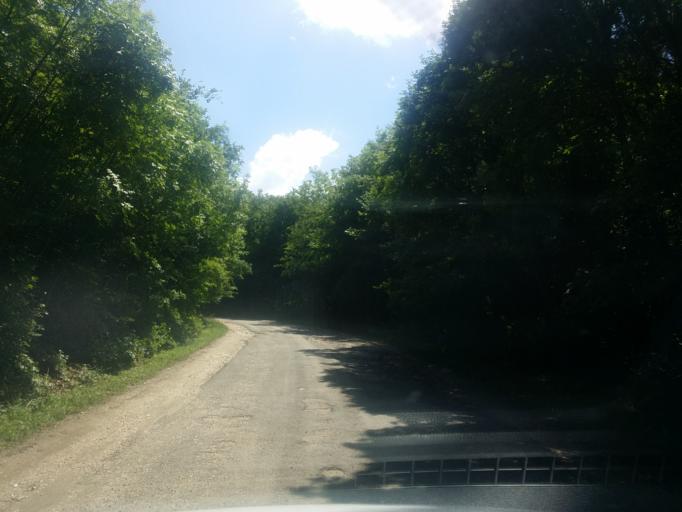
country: HU
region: Komarom-Esztergom
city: Piliscsev
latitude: 47.7052
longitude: 18.8286
